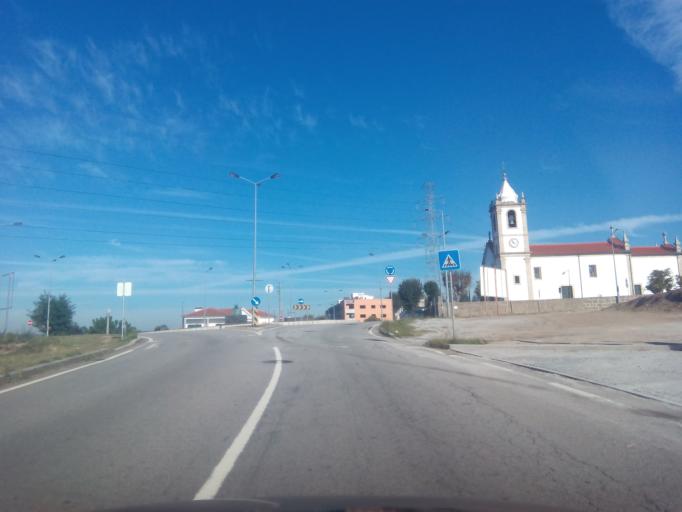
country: PT
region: Porto
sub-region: Paredes
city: Gandra
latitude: 41.2004
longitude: -8.4395
